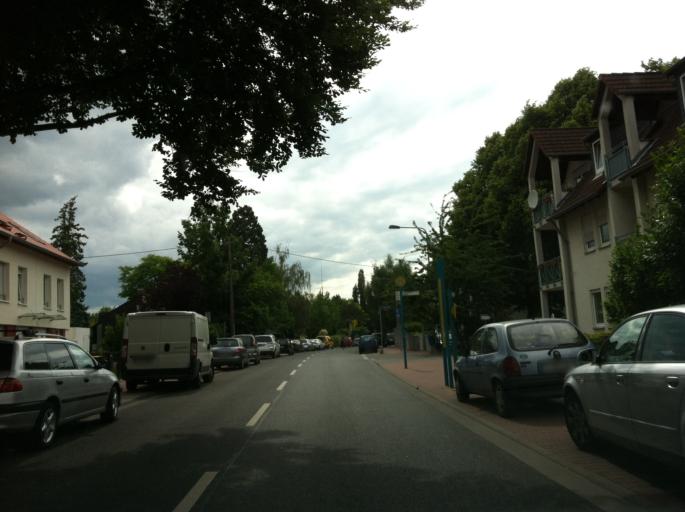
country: DE
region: Hesse
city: Kelsterbach
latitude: 50.0766
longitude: 8.5106
